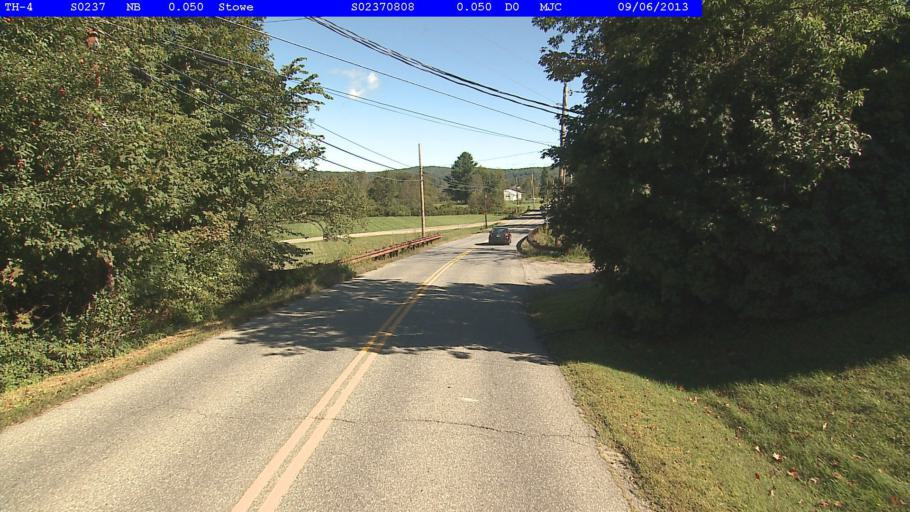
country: US
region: Vermont
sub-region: Lamoille County
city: Morristown
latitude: 44.4826
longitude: -72.6643
